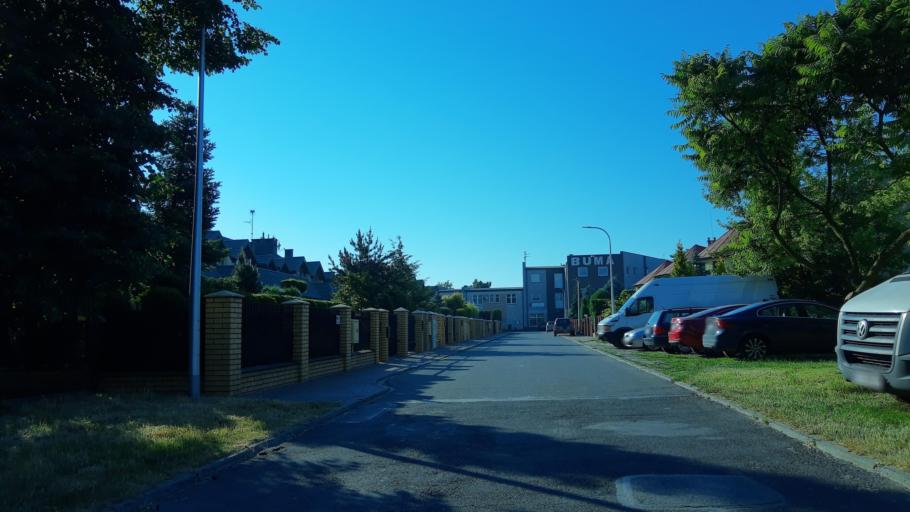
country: PL
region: Lodz Voivodeship
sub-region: Powiat sieradzki
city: Sieradz
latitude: 51.5859
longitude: 18.7178
